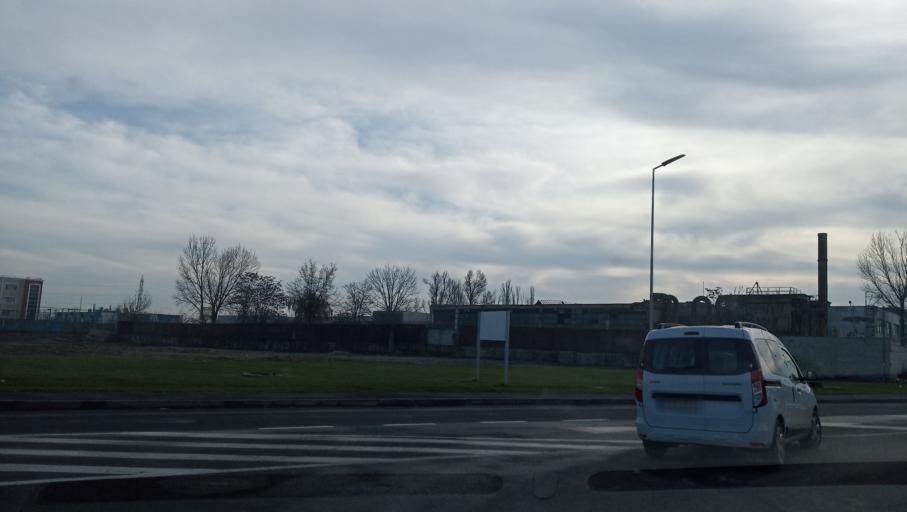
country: RO
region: Ilfov
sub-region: Comuna Glina
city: Catelu
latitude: 44.4091
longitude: 26.2083
